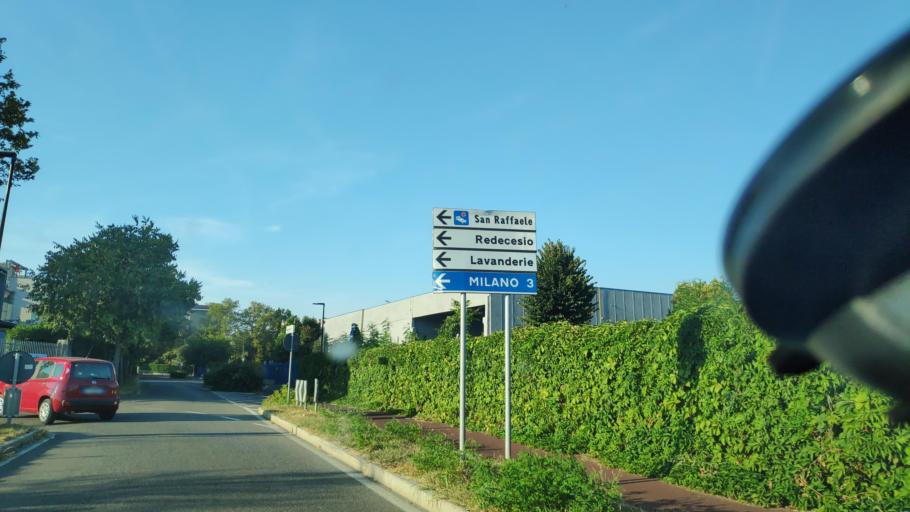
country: IT
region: Lombardy
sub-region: Citta metropolitana di Milano
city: Segrate
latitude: 45.4856
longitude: 9.2970
